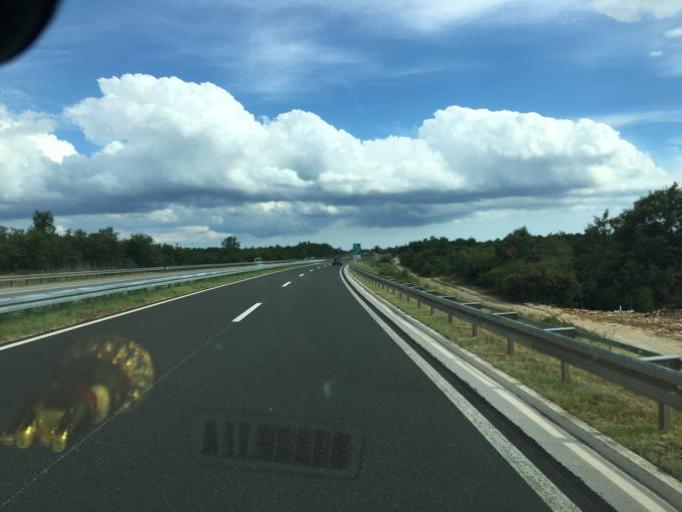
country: HR
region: Istarska
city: Vodnjan
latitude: 45.0842
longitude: 13.8368
